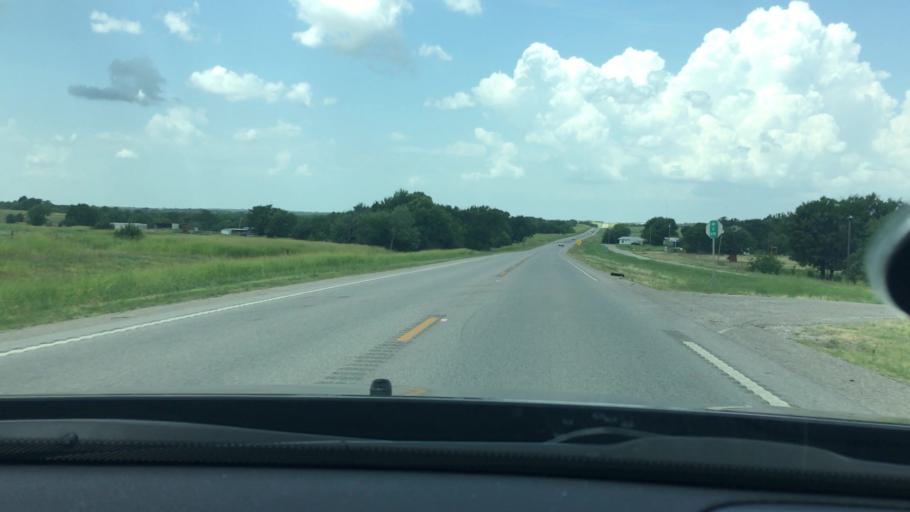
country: US
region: Oklahoma
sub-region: Marshall County
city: Oakland
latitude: 34.1001
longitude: -96.8406
